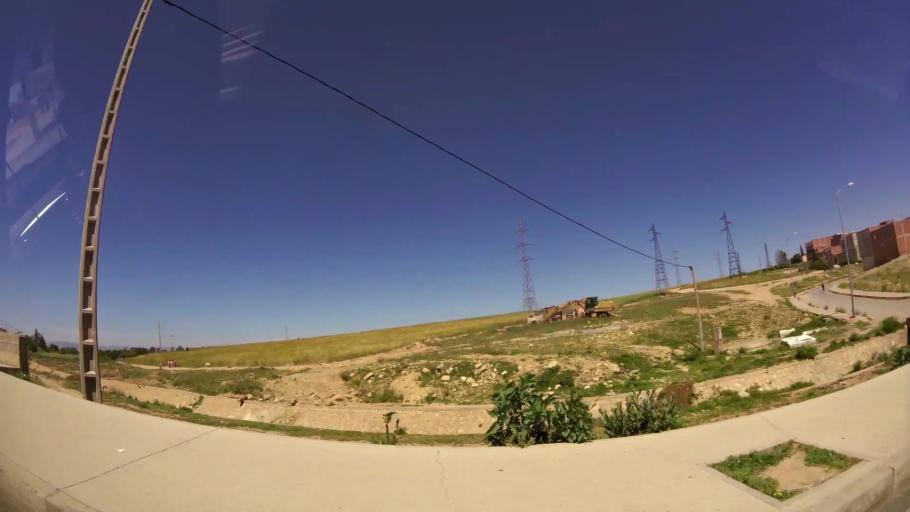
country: MA
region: Oriental
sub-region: Oujda-Angad
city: Oujda
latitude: 34.6556
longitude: -1.8664
